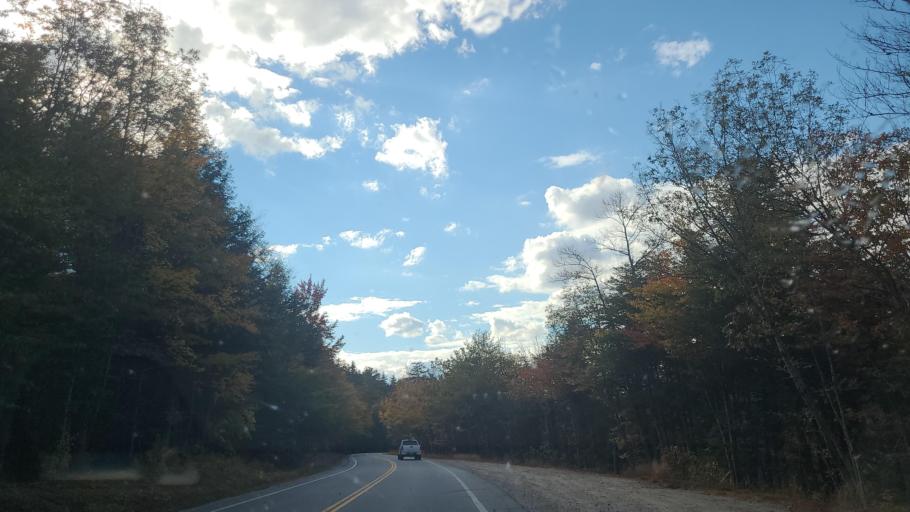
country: US
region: New Hampshire
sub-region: Carroll County
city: Conway
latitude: 43.9903
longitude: -71.1909
